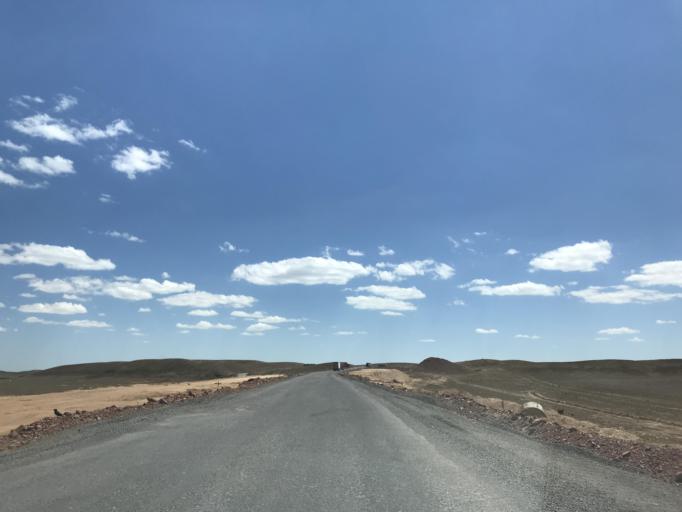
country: KZ
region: Almaty Oblysy
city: Ulken
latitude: 45.0663
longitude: 73.9972
